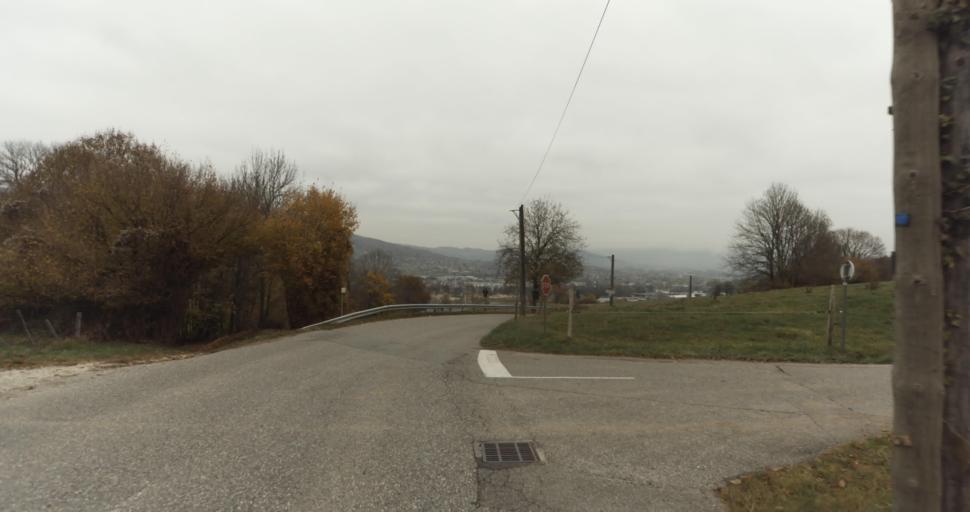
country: FR
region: Rhone-Alpes
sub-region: Departement de la Haute-Savoie
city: Poisy
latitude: 45.9332
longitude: 6.0626
